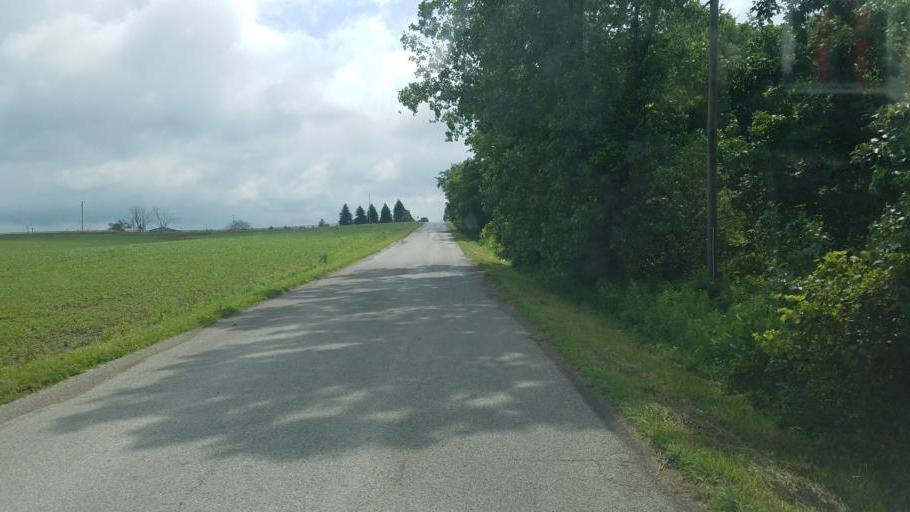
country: US
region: Ohio
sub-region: Richland County
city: Lexington
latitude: 40.6808
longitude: -82.6482
